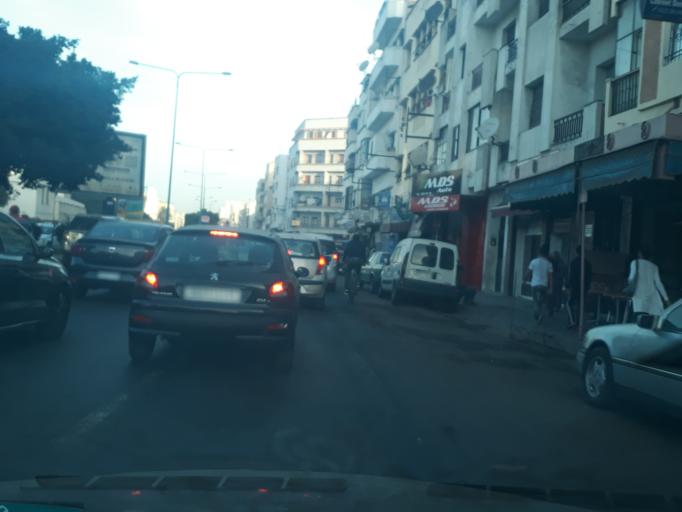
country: MA
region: Grand Casablanca
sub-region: Casablanca
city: Casablanca
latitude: 33.5783
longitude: -7.6340
